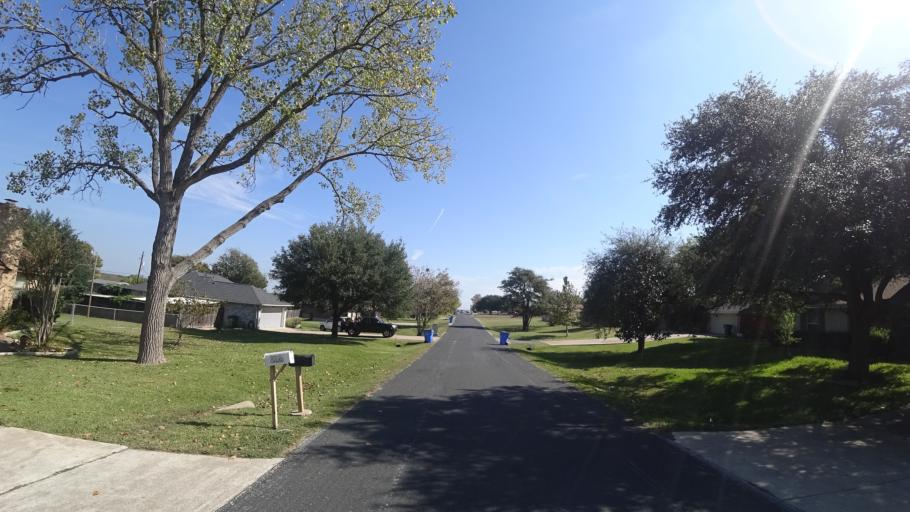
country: US
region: Texas
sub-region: Travis County
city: Pflugerville
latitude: 30.4165
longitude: -97.6266
